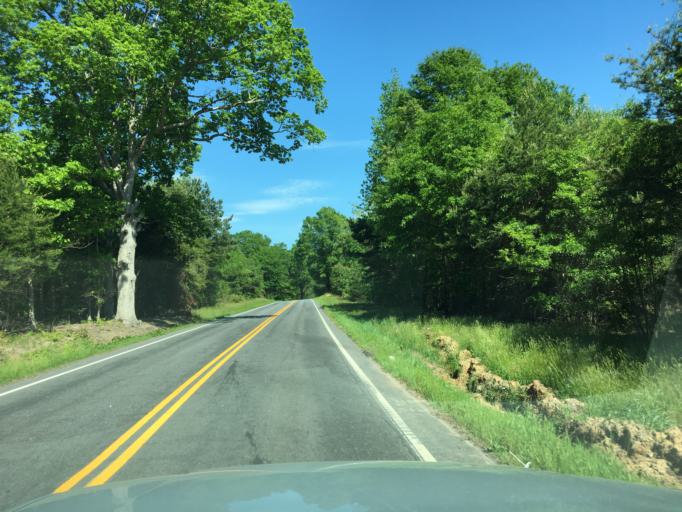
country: US
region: South Carolina
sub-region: Spartanburg County
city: Southern Shops
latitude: 34.9901
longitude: -82.0281
